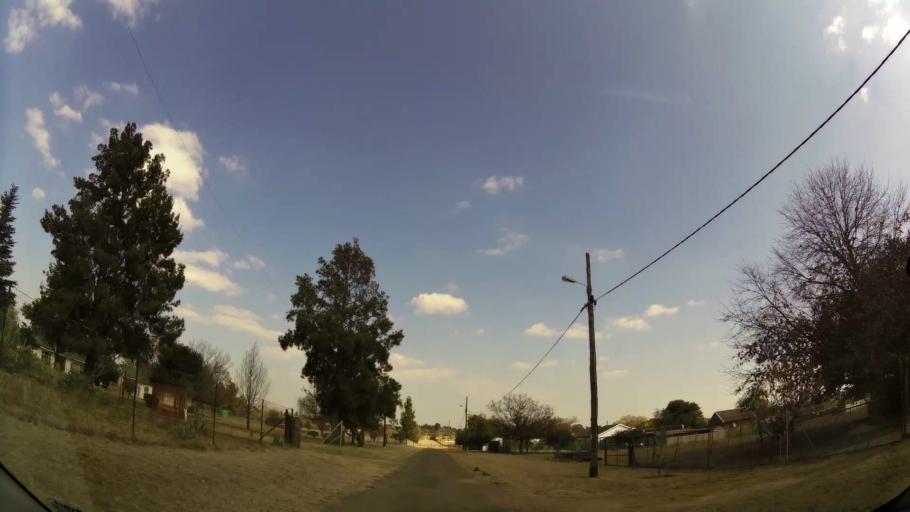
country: ZA
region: Gauteng
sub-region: Ekurhuleni Metropolitan Municipality
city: Benoni
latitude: -26.0778
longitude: 28.3403
